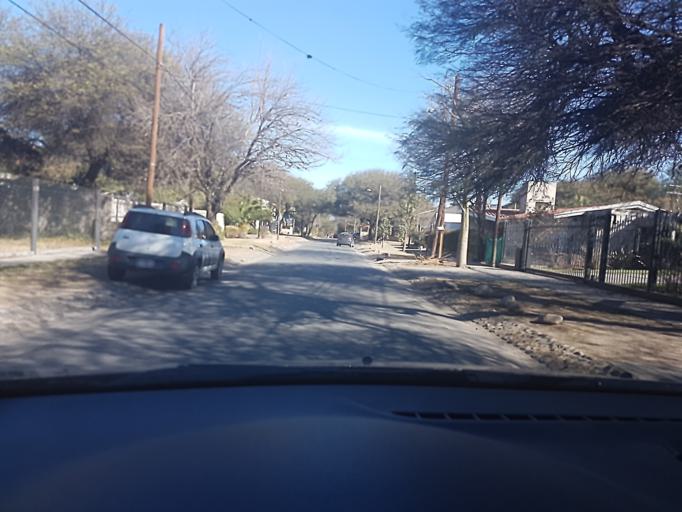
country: AR
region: Cordoba
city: Villa Allende
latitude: -31.3507
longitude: -64.2520
